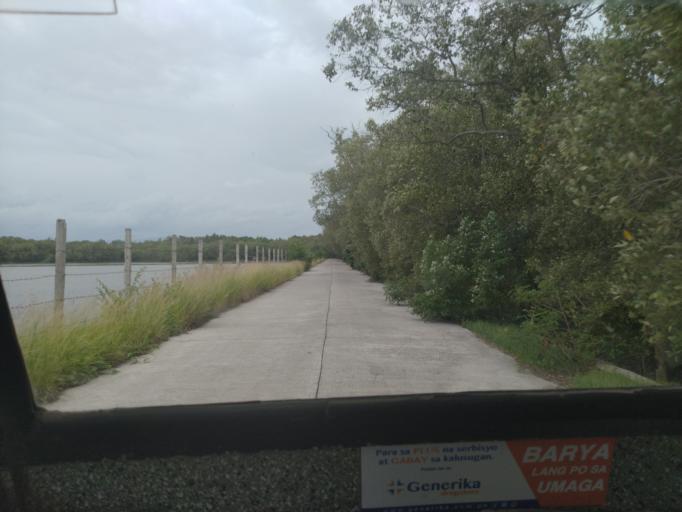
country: PH
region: Central Visayas
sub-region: Province of Negros Oriental
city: Okiot
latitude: 9.5441
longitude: 123.1537
